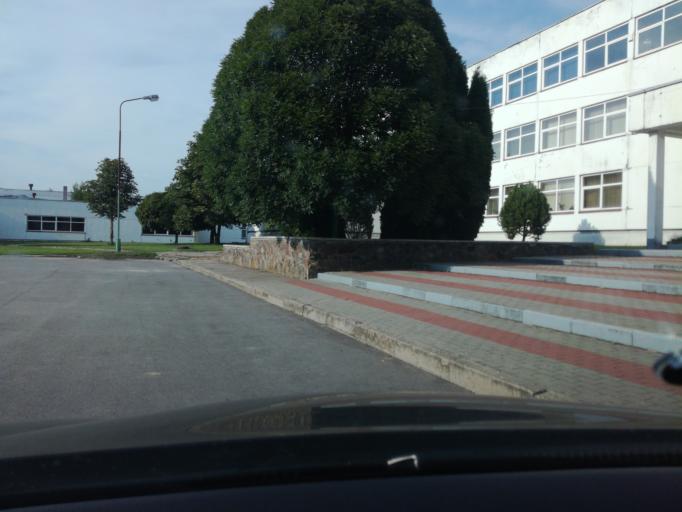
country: LT
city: Simnas
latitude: 54.3816
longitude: 23.6554
